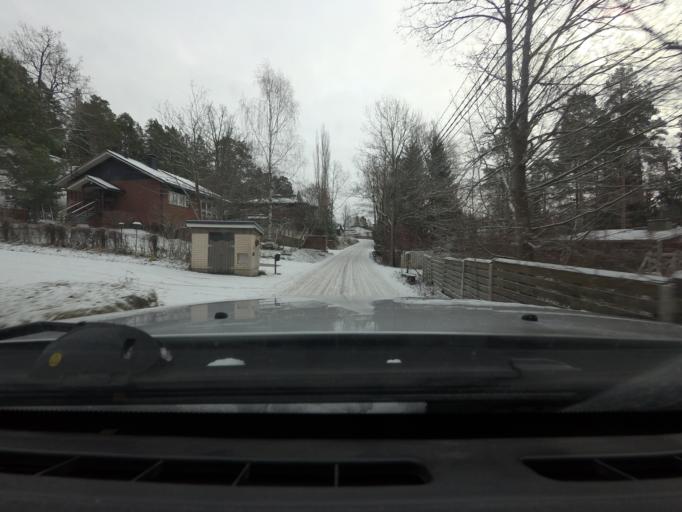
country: FI
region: Uusimaa
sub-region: Helsinki
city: Kilo
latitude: 60.2232
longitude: 24.7675
